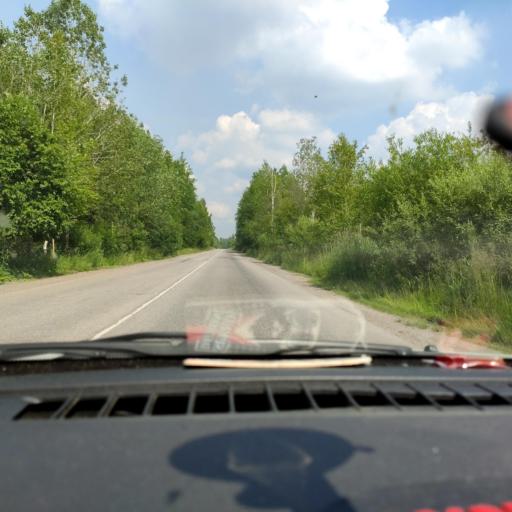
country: RU
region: Perm
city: Novyye Lyady
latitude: 57.9349
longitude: 56.4828
